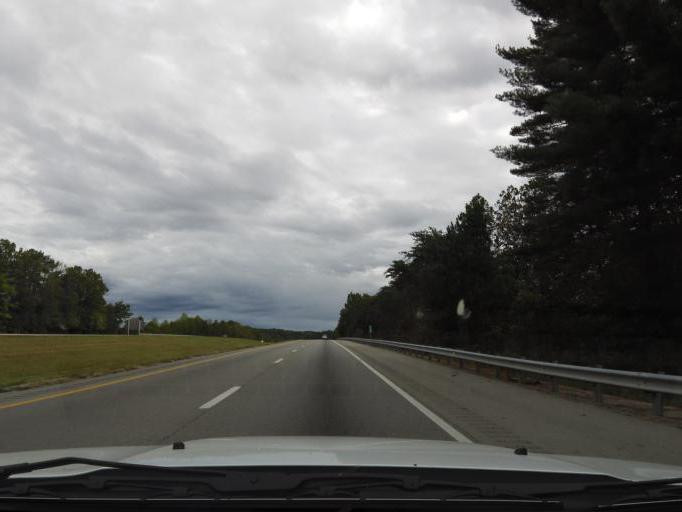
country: US
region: Kentucky
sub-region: Whitley County
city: Williamsburg
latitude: 36.8289
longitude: -84.1638
